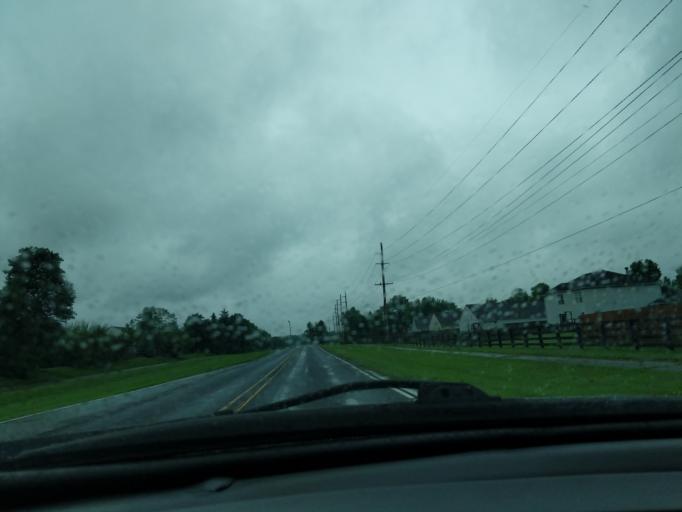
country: US
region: Indiana
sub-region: Hamilton County
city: Noblesville
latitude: 40.0675
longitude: -86.0335
